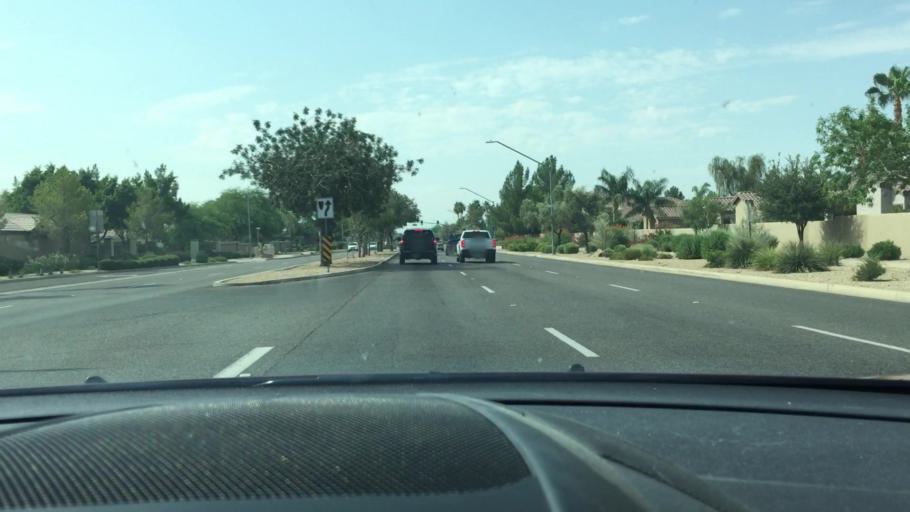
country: US
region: Arizona
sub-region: Maricopa County
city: Peoria
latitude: 33.6740
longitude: -112.2031
